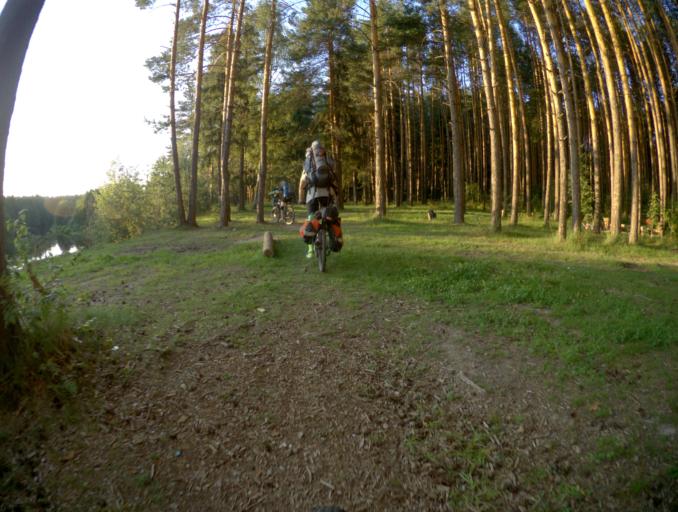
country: RU
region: Nizjnij Novgorod
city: Sitniki
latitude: 56.4683
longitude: 44.0181
